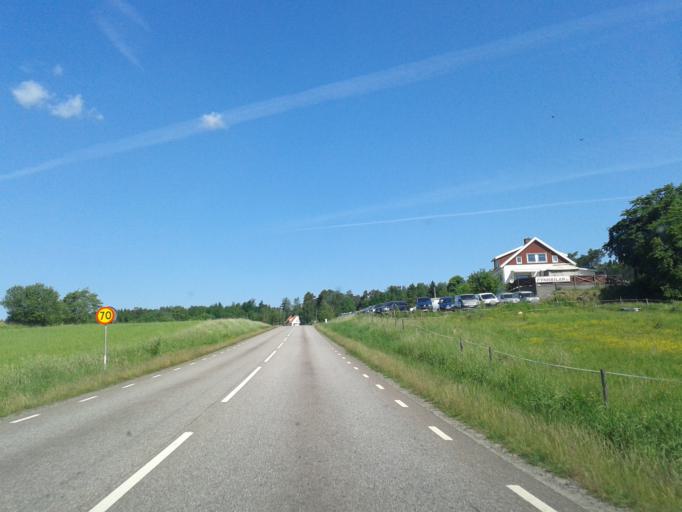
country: SE
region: Vaestra Goetaland
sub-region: Kungalvs Kommun
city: Kode
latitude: 57.9194
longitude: 11.9169
